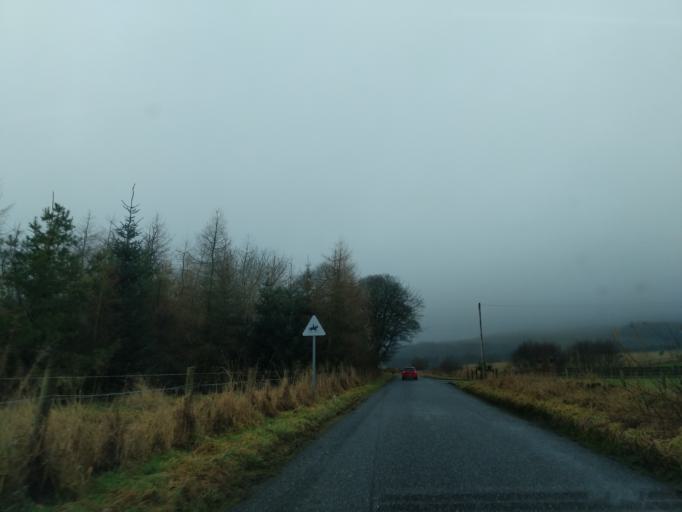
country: GB
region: Scotland
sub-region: Fife
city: Saline
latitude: 56.1962
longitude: -3.5631
